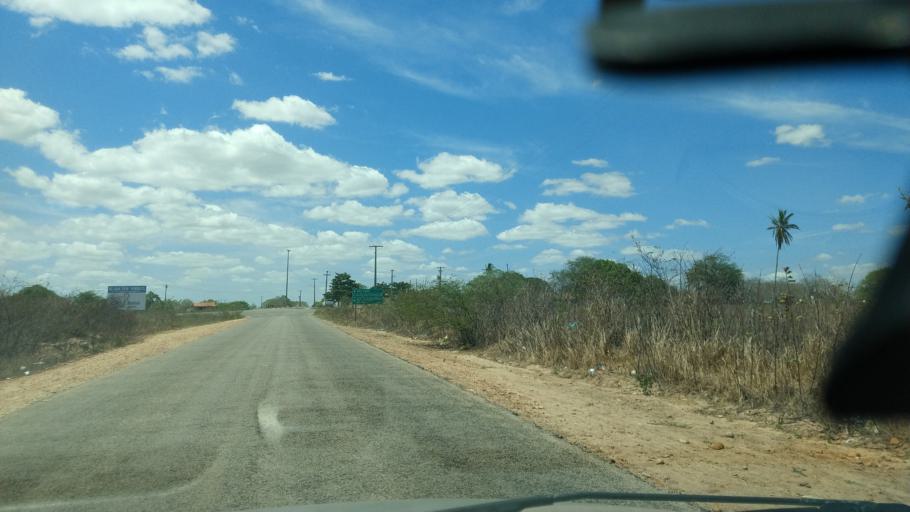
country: BR
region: Rio Grande do Norte
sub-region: Sao Paulo Do Potengi
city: Sao Paulo do Potengi
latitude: -5.9137
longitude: -35.7517
